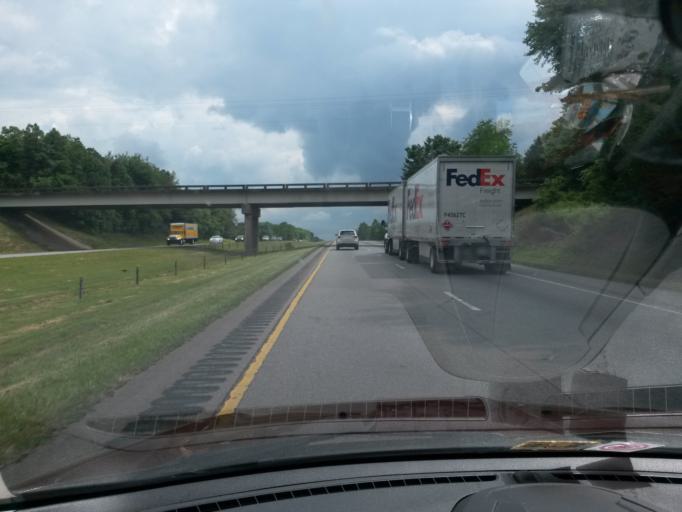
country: US
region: North Carolina
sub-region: Iredell County
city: Statesville
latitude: 35.9602
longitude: -80.8471
